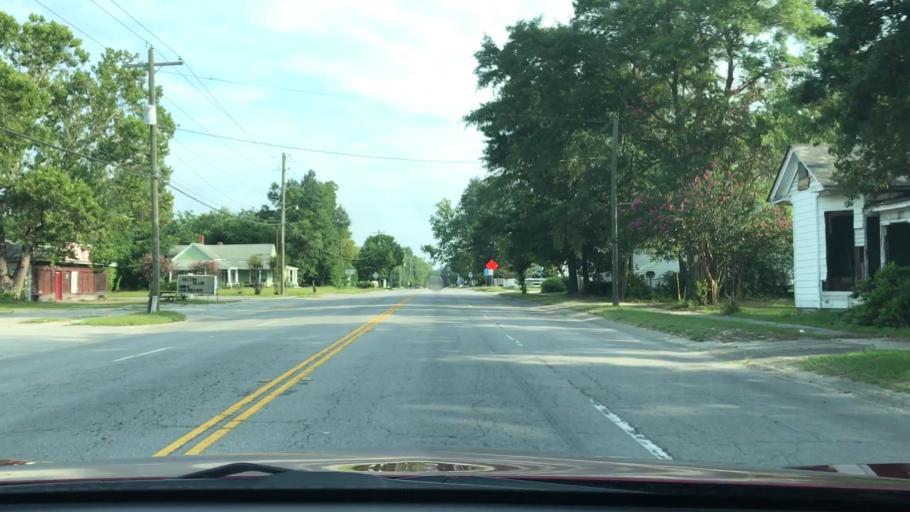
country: US
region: South Carolina
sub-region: Bamberg County
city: Denmark
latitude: 33.5314
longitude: -81.1230
